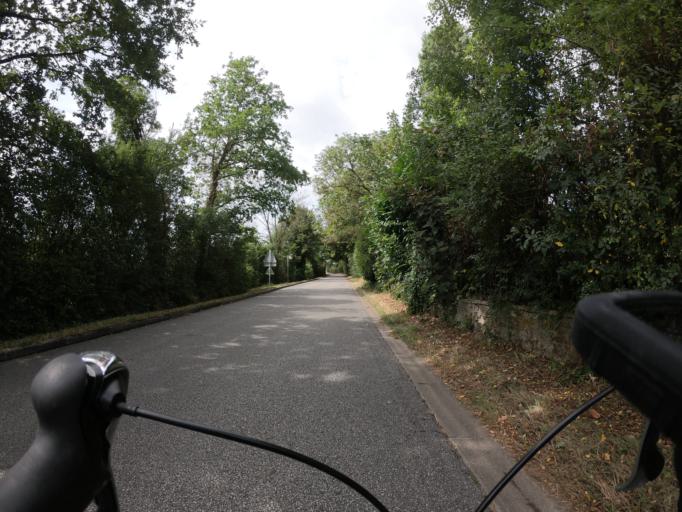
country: FR
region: Ile-de-France
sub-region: Departement des Yvelines
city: Magny-les-Hameaux
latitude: 48.7458
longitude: 2.0561
